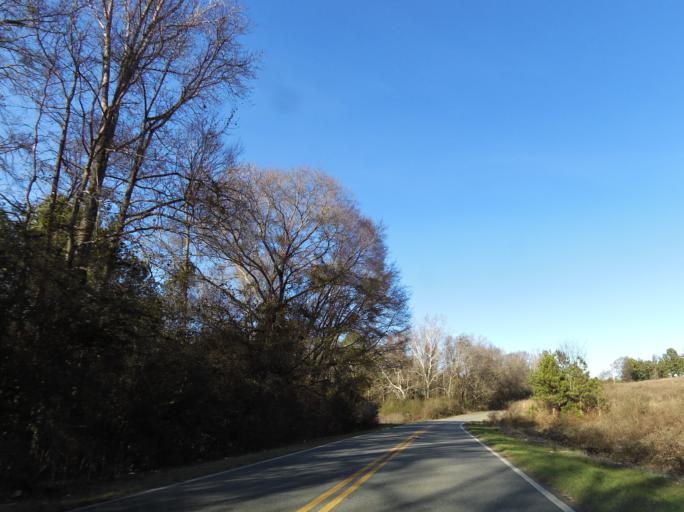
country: US
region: Georgia
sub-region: Bibb County
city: West Point
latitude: 32.7664
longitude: -83.8381
